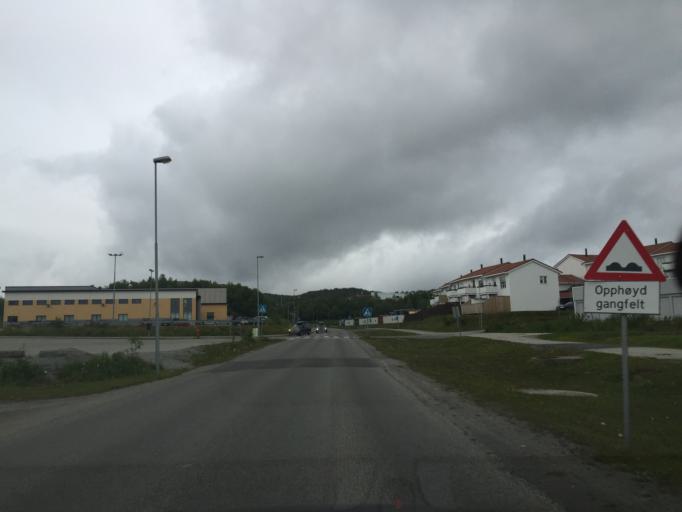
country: NO
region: Nordland
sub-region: Bodo
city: Lopsmarka
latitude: 67.2881
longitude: 14.5710
